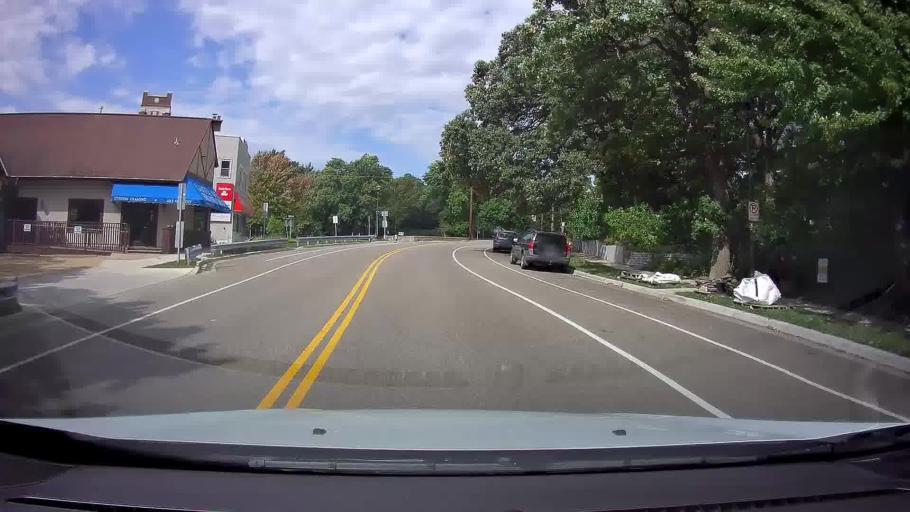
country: US
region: Minnesota
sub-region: Ramsey County
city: Lauderdale
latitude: 44.9793
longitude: -93.1925
